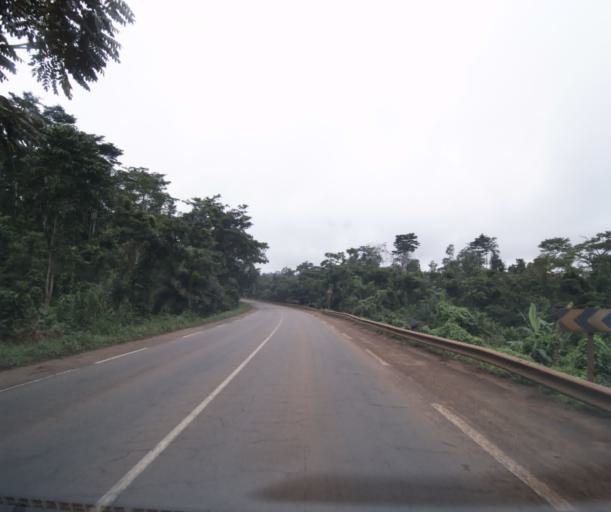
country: CM
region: Centre
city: Mbankomo
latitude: 3.7636
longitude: 11.0986
